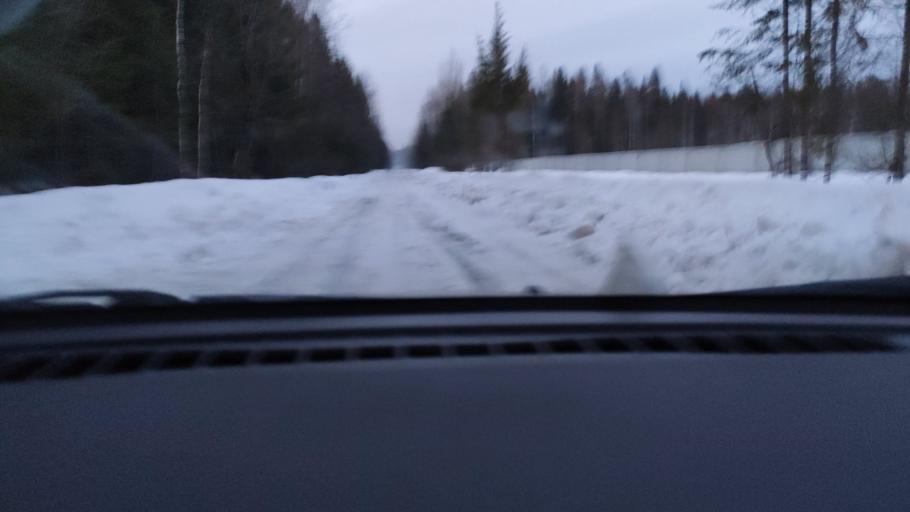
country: RU
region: Perm
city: Kondratovo
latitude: 58.0710
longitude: 56.1279
